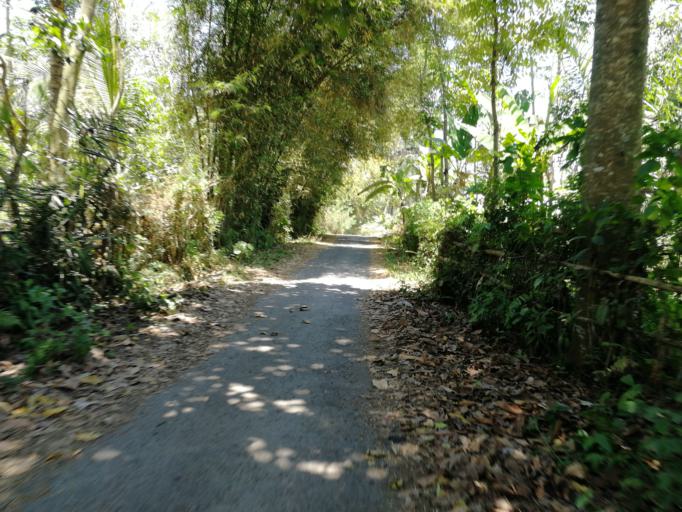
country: ID
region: West Nusa Tenggara
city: Tetebatu
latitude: -8.5493
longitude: 116.4192
